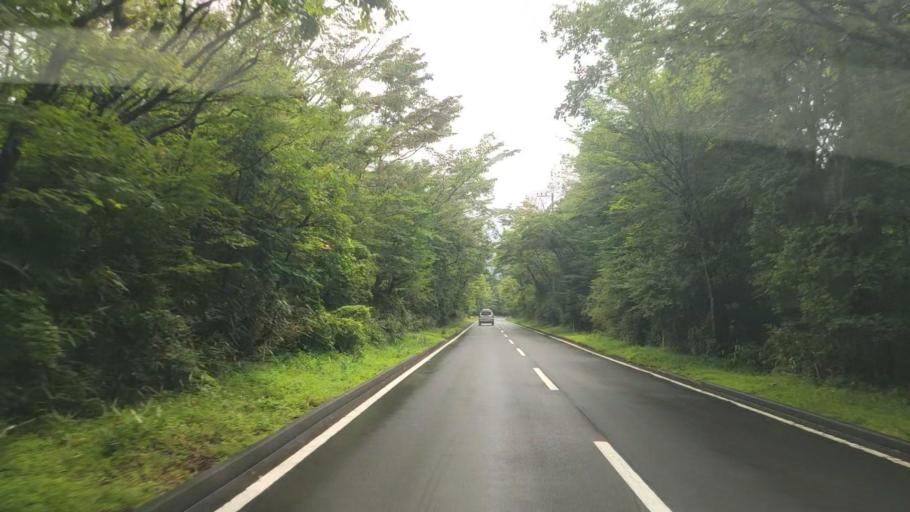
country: JP
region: Shizuoka
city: Gotemba
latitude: 35.2734
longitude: 138.7970
